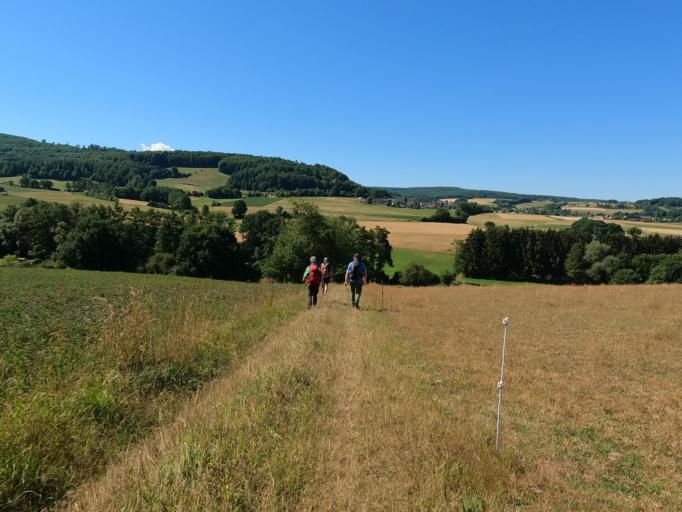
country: DE
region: Hesse
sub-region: Regierungsbezirk Darmstadt
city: Schluchtern
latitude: 50.3154
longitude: 9.5141
